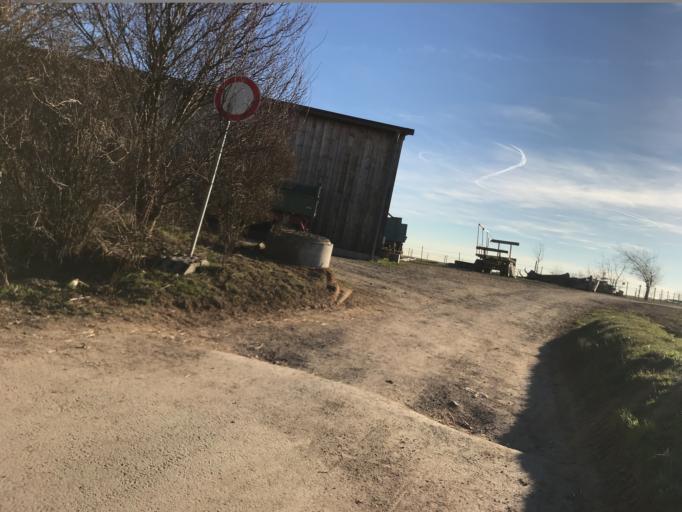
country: DE
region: Rheinland-Pfalz
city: Mainz
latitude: 49.9611
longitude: 8.3006
